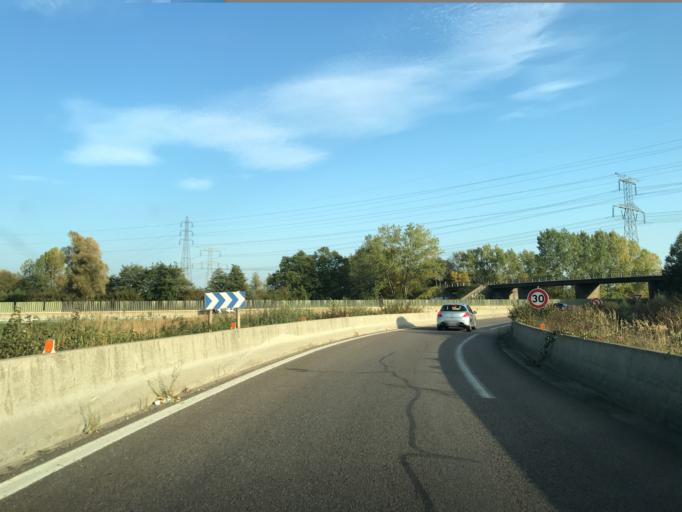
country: FR
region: Lorraine
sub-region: Departement de la Moselle
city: Maizieres-les-Metz
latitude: 49.1993
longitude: 6.1743
